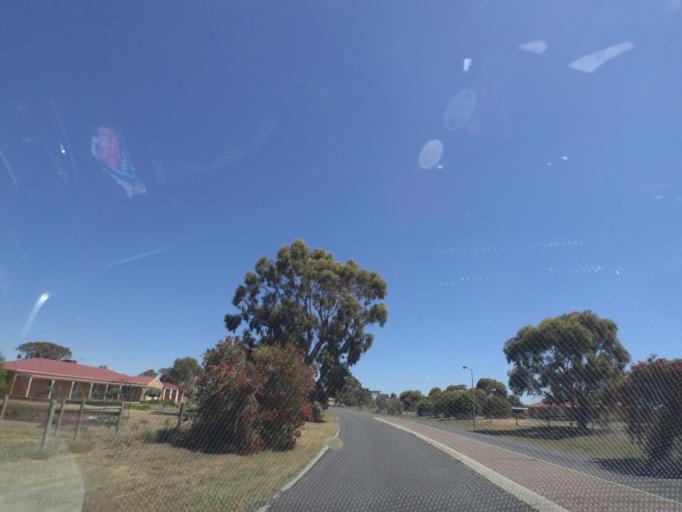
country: AU
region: Victoria
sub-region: Melton
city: Brookfield
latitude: -37.6958
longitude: 144.5004
